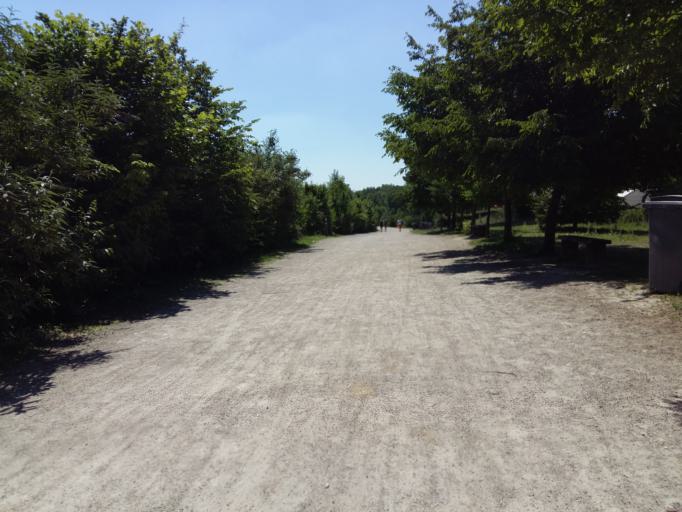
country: FR
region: Rhone-Alpes
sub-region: Departement de l'Ain
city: Miribel
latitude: 45.8131
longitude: 4.9579
